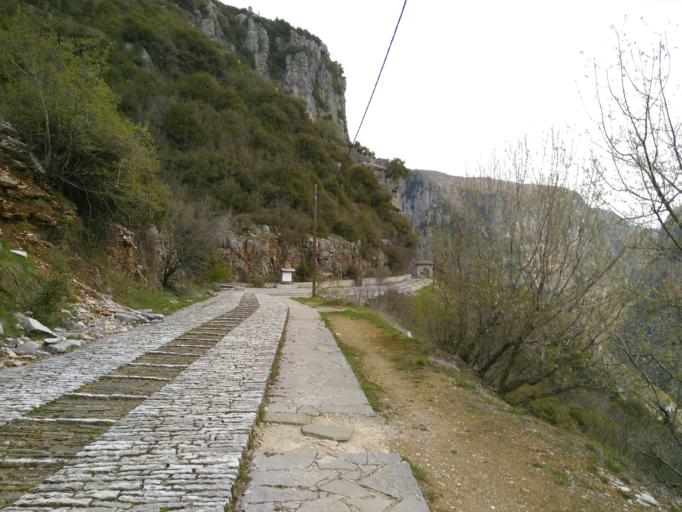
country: GR
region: Epirus
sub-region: Nomos Ioanninon
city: Asprangeloi
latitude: 39.8855
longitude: 20.7523
